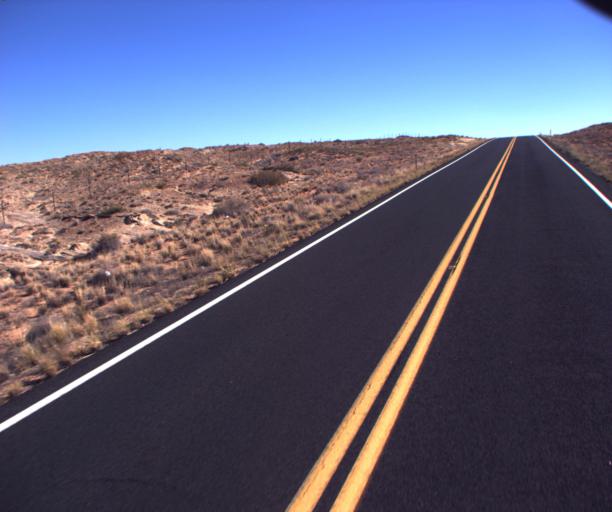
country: US
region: Arizona
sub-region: Coconino County
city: Tuba City
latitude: 36.0198
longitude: -111.1190
